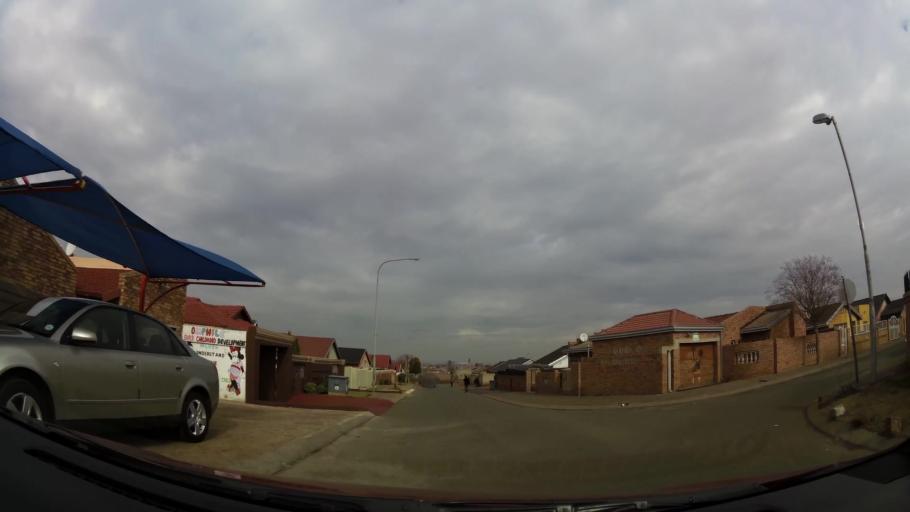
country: ZA
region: Gauteng
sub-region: City of Johannesburg Metropolitan Municipality
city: Soweto
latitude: -26.2783
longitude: 27.8346
